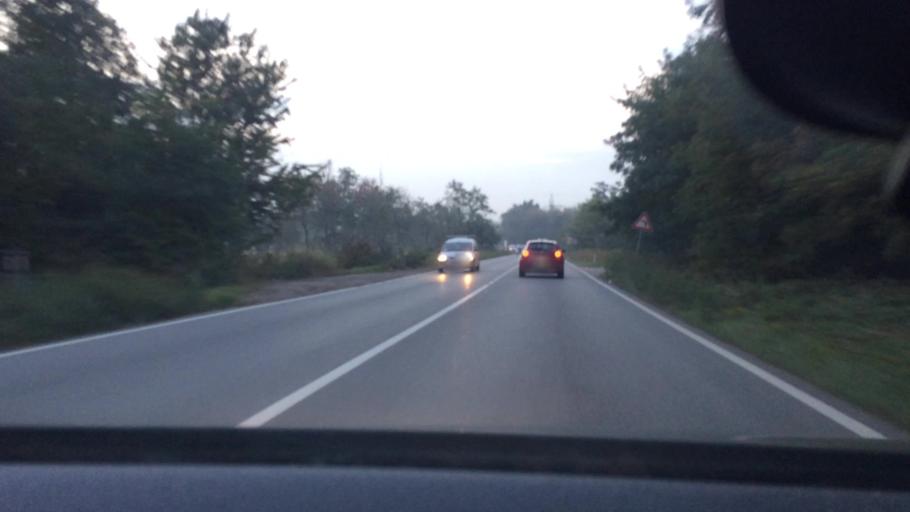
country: IT
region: Lombardy
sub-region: Citta metropolitana di Milano
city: Nerviano
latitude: 45.5327
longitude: 8.9687
